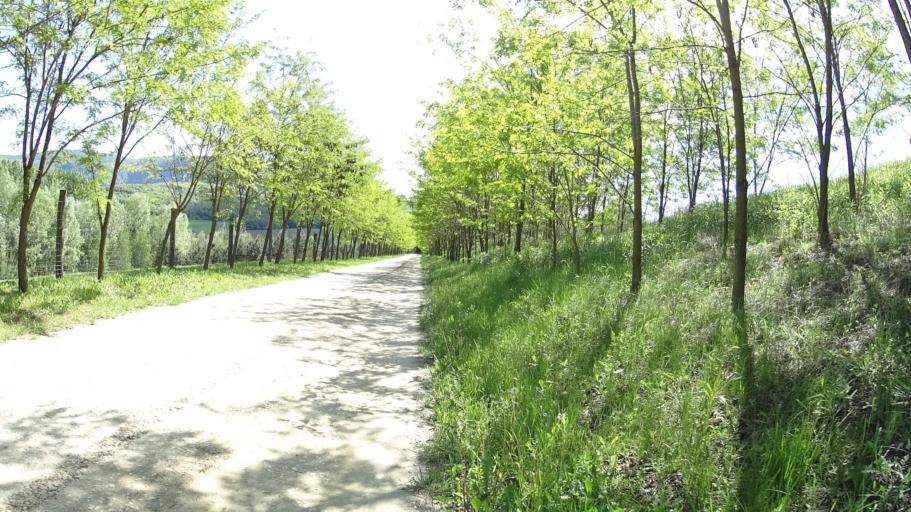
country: HU
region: Komarom-Esztergom
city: Kesztolc
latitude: 47.6982
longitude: 18.8047
